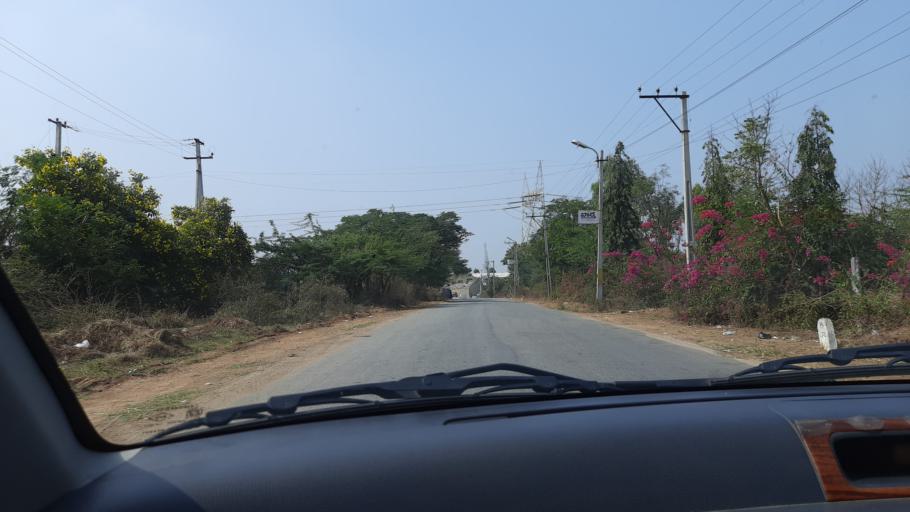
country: IN
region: Telangana
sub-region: Rangareddi
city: Lal Bahadur Nagar
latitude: 17.2804
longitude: 78.6502
